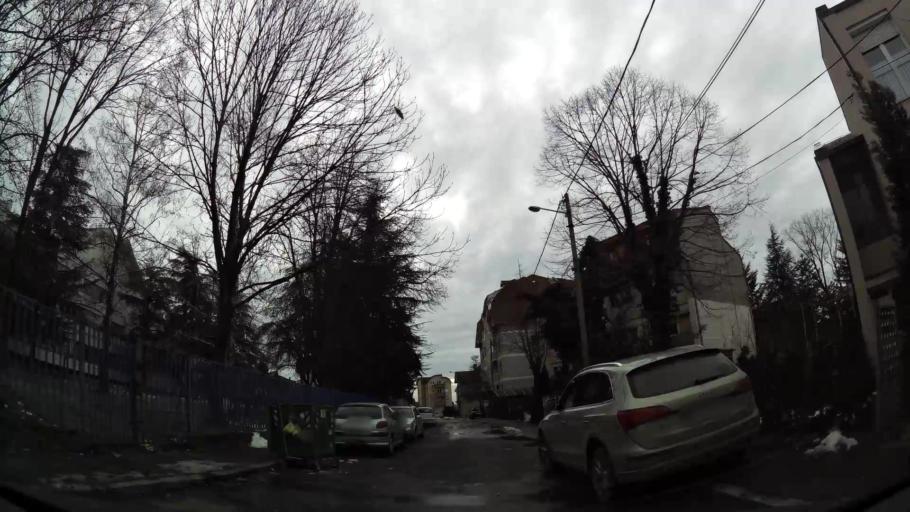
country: RS
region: Central Serbia
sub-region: Belgrade
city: Cukarica
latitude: 44.7609
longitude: 20.4115
